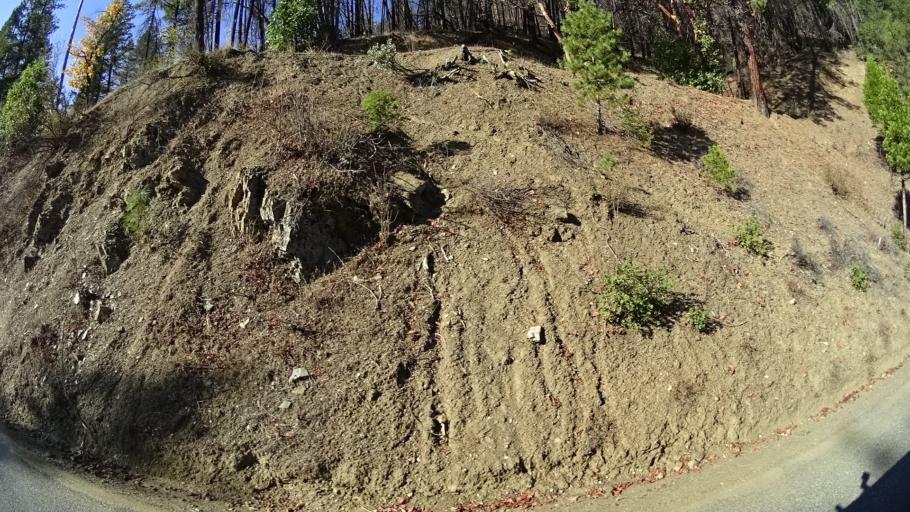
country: US
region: California
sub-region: Siskiyou County
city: Happy Camp
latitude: 41.7045
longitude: -123.0384
